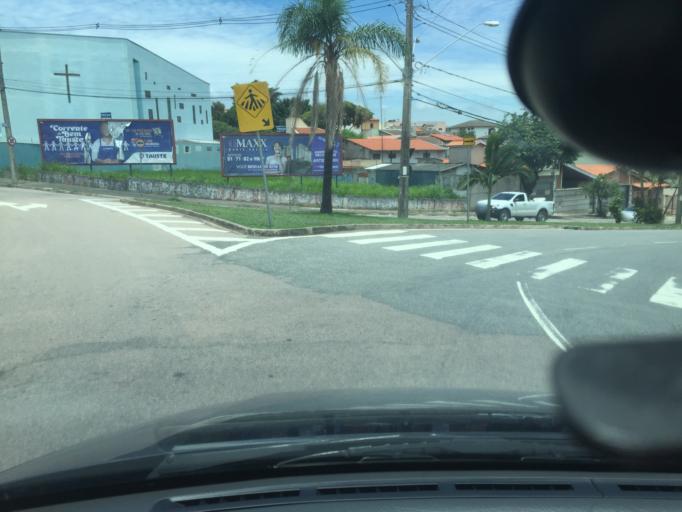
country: BR
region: Sao Paulo
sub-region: Jundiai
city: Jundiai
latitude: -23.1637
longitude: -46.8978
